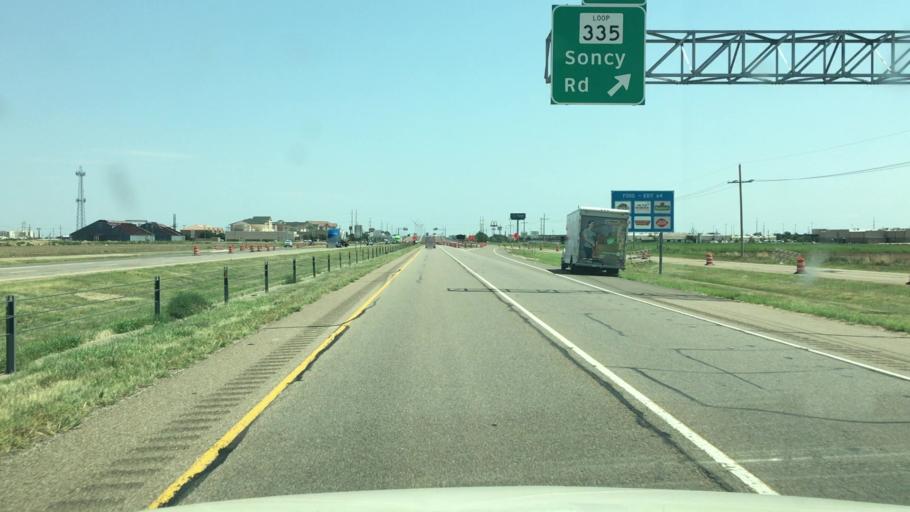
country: US
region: Texas
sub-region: Potter County
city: Bushland
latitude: 35.1873
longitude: -101.9484
